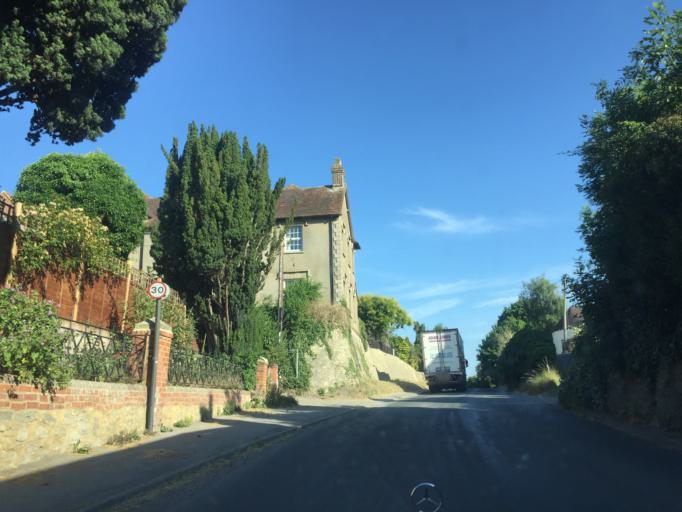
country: GB
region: England
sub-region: Oxfordshire
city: Thame
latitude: 51.7099
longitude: -1.0058
